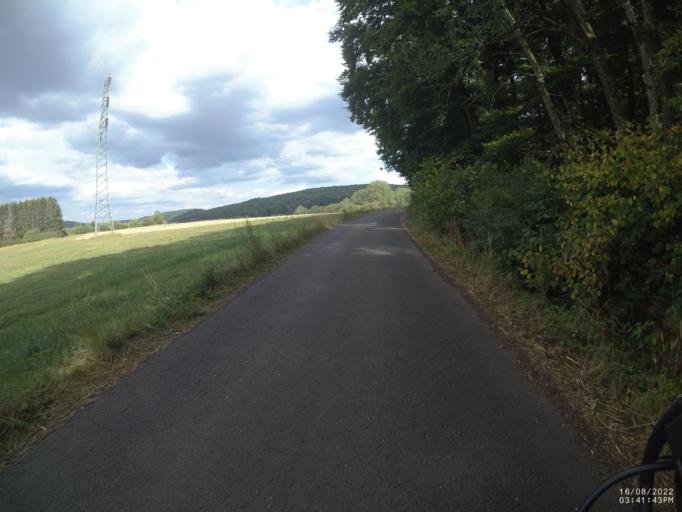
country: DE
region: Rheinland-Pfalz
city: Berndorf
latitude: 50.2919
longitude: 6.7083
